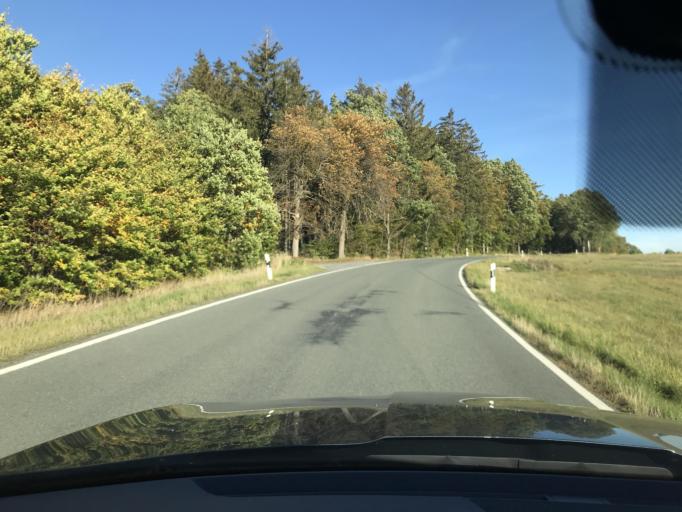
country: DE
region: Saxony-Anhalt
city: Friedrichsbrunn
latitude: 51.6827
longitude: 11.0122
